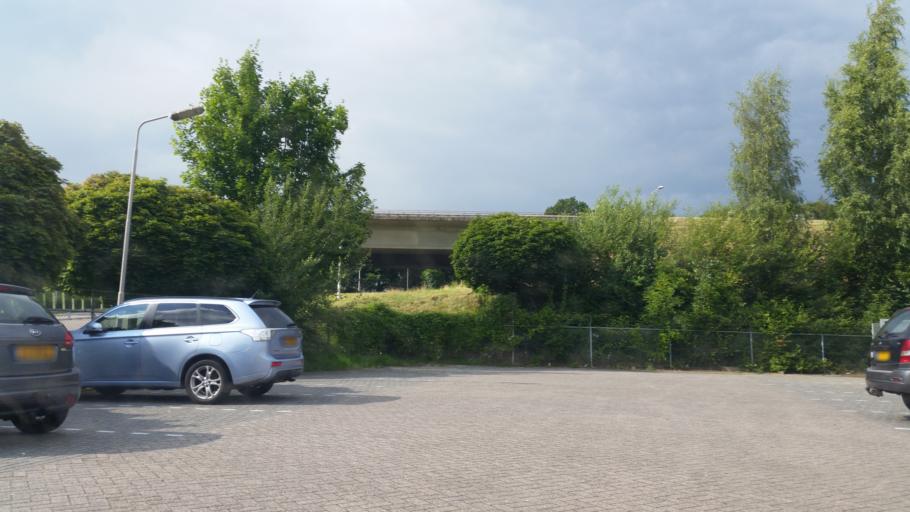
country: NL
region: Limburg
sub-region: Valkenburg aan de Geul
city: Broekhem
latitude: 50.8734
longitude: 5.8161
